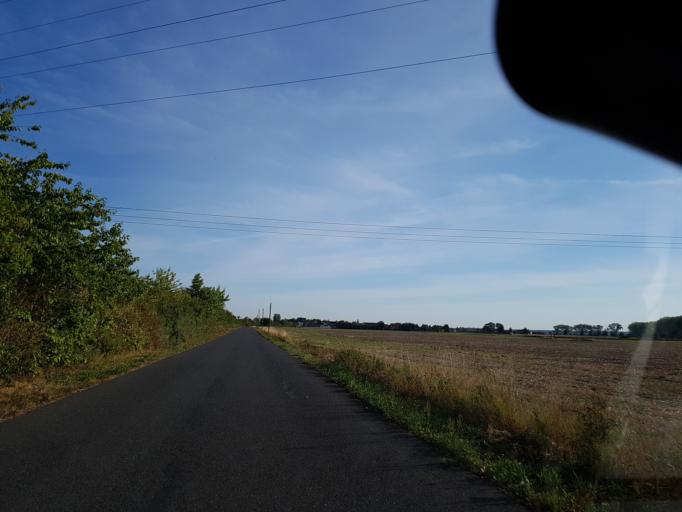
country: DE
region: Saxony
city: Nauwalde
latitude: 51.4510
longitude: 13.4207
